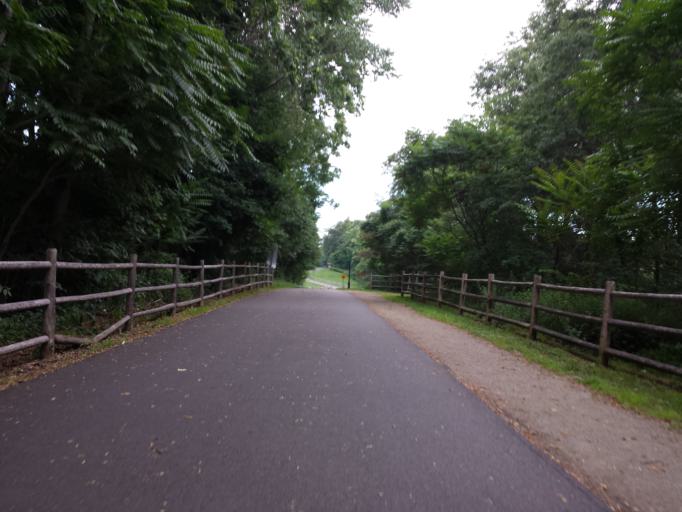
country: US
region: New York
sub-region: Dutchess County
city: Myers Corner
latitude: 41.6248
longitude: -73.8533
